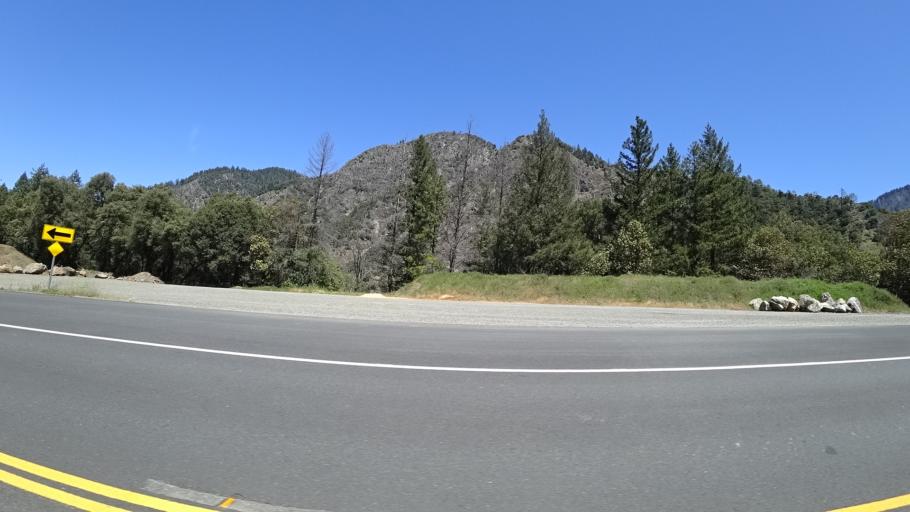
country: US
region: California
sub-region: Humboldt County
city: Willow Creek
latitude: 40.8495
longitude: -123.4839
